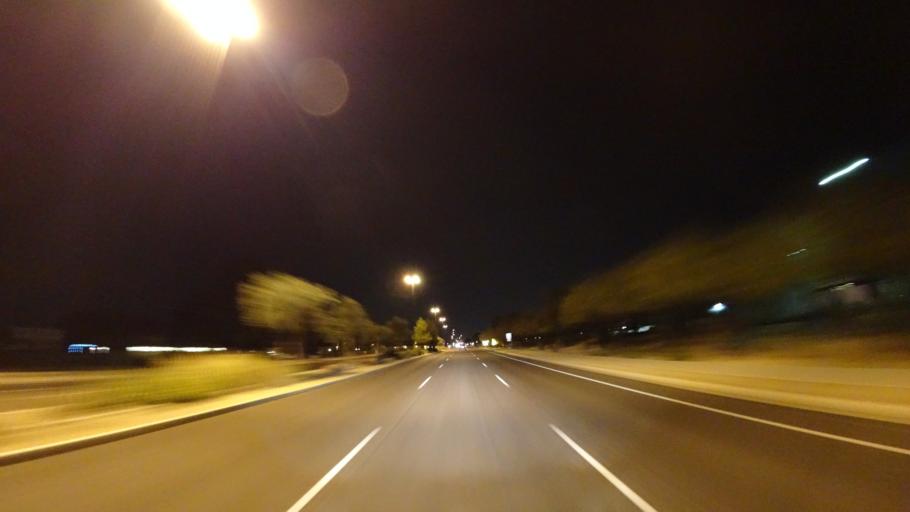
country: US
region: Arizona
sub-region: Maricopa County
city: Gilbert
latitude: 33.3794
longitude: -111.7097
